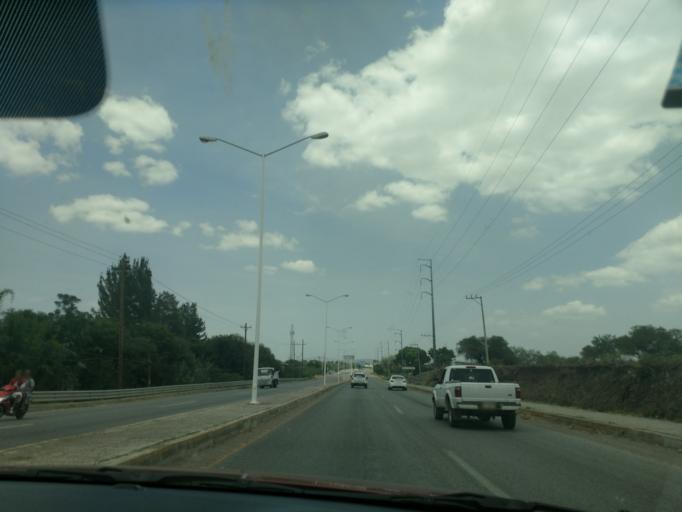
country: MX
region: San Luis Potosi
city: Rio Verde
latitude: 21.9218
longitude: -99.9680
